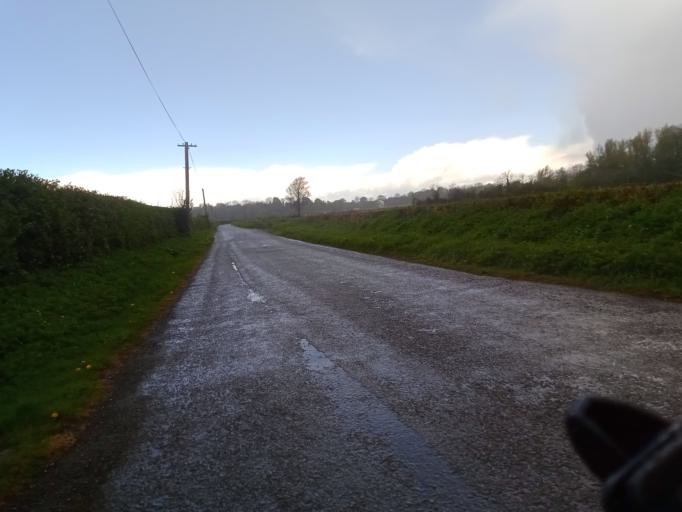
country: IE
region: Leinster
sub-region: Kilkenny
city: Kilkenny
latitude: 52.6886
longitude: -7.2704
